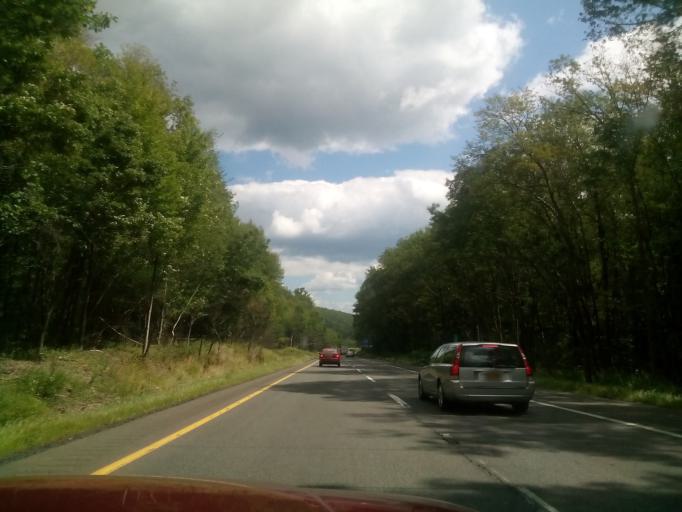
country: US
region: Pennsylvania
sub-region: Monroe County
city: Tannersville
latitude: 41.0570
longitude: -75.3235
